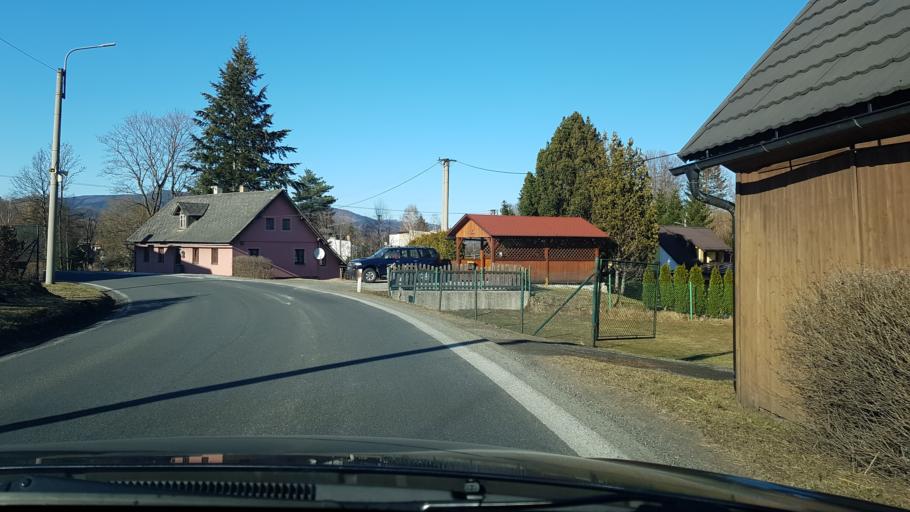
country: CZ
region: Olomoucky
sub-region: Okres Jesenik
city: Jesenik
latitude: 50.1928
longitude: 17.1954
